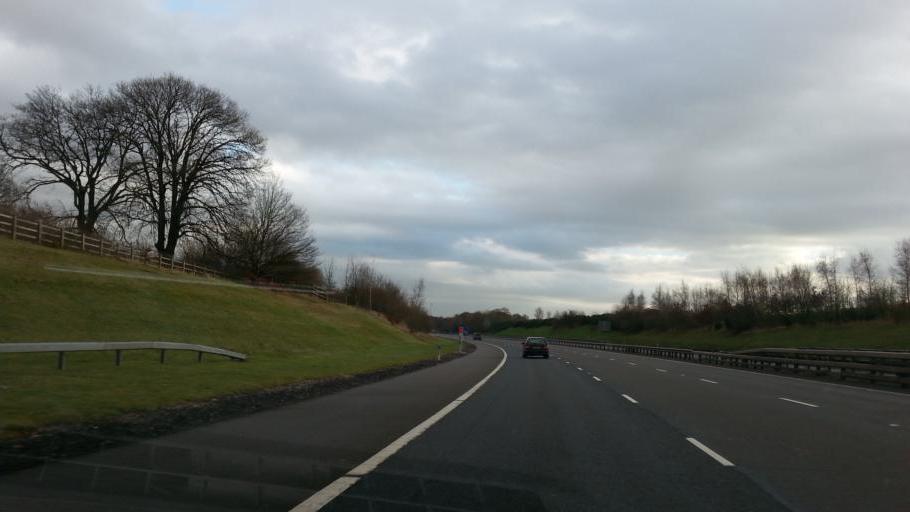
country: GB
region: England
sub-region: City and Borough of Birmingham
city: Sutton Coldfield
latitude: 52.5832
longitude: -1.7888
